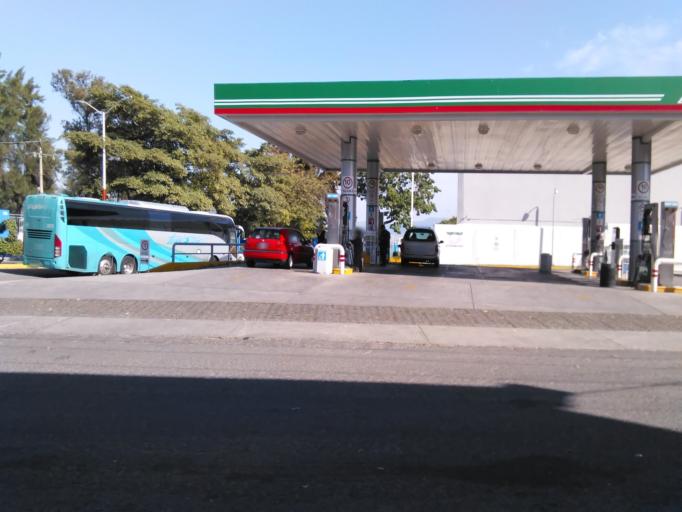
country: MX
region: Nayarit
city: Tepic
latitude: 21.4879
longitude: -104.8911
